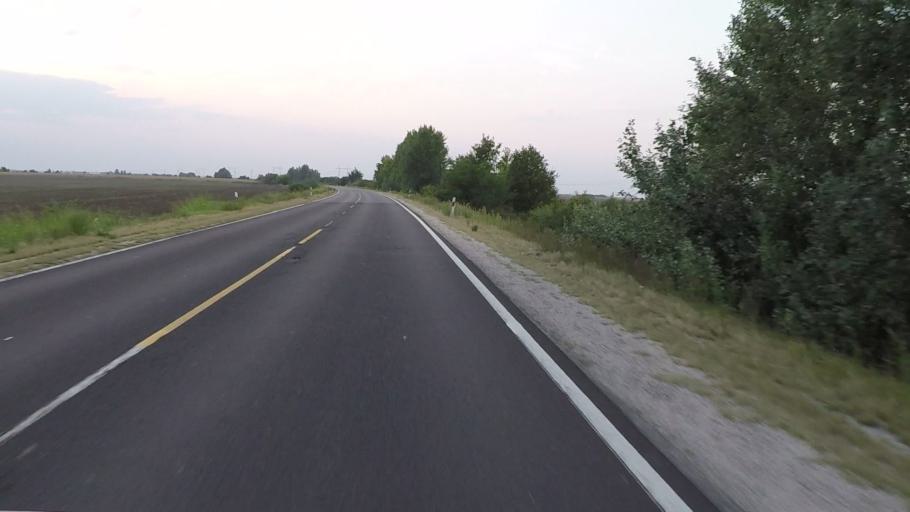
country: HU
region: Pest
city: Abony
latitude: 47.2096
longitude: 20.0669
